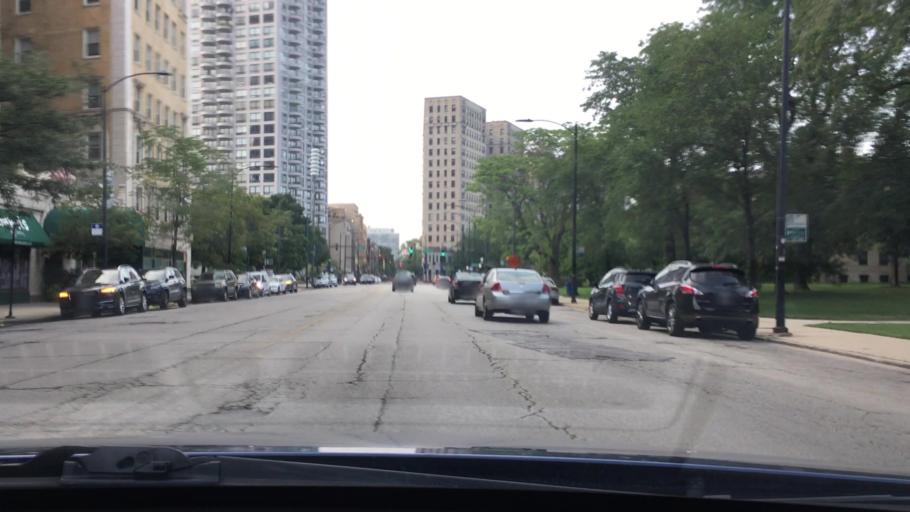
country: US
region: Illinois
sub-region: Cook County
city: Chicago
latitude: 41.9174
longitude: -87.6354
